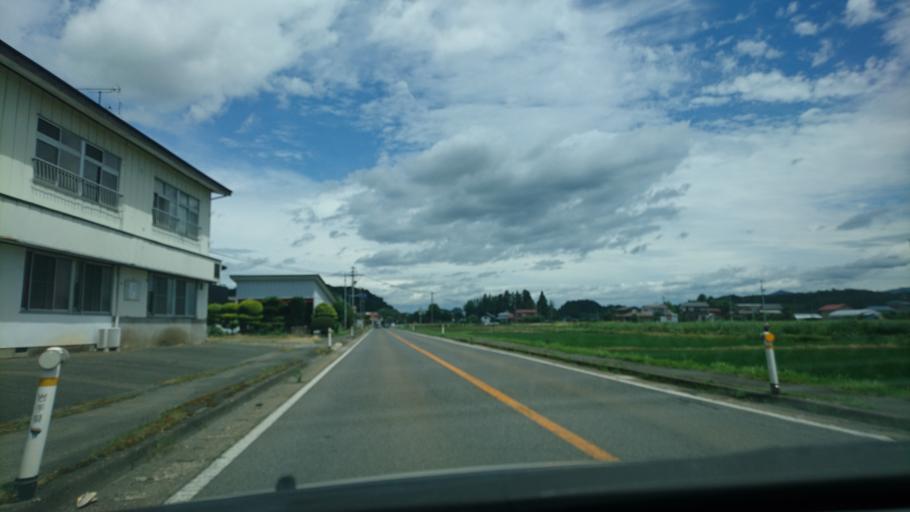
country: JP
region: Iwate
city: Morioka-shi
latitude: 39.5536
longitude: 141.1783
